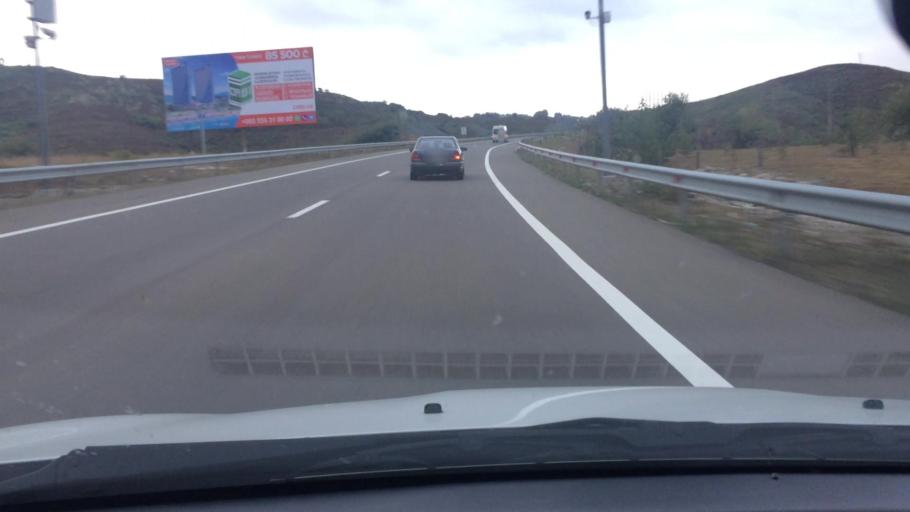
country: GE
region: Ajaria
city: Makhinjauri
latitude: 41.7248
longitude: 41.7495
